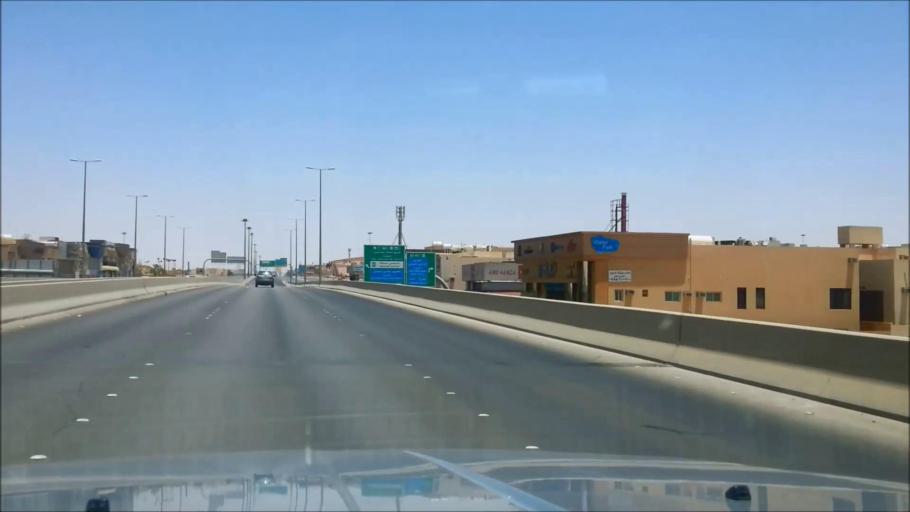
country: SA
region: Ar Riyad
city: Riyadh
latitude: 24.7639
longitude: 46.6716
